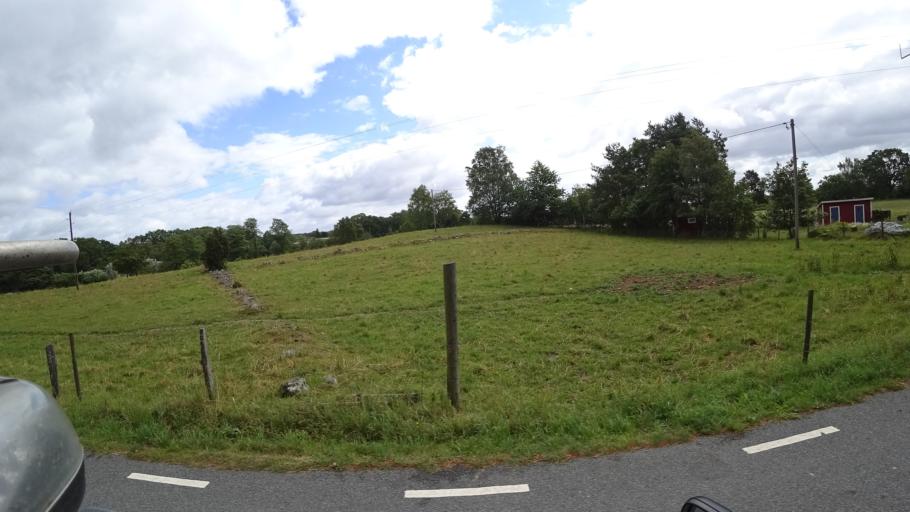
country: SE
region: Skane
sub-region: Kristianstads Kommun
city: Degeberga
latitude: 55.7287
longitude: 14.0000
